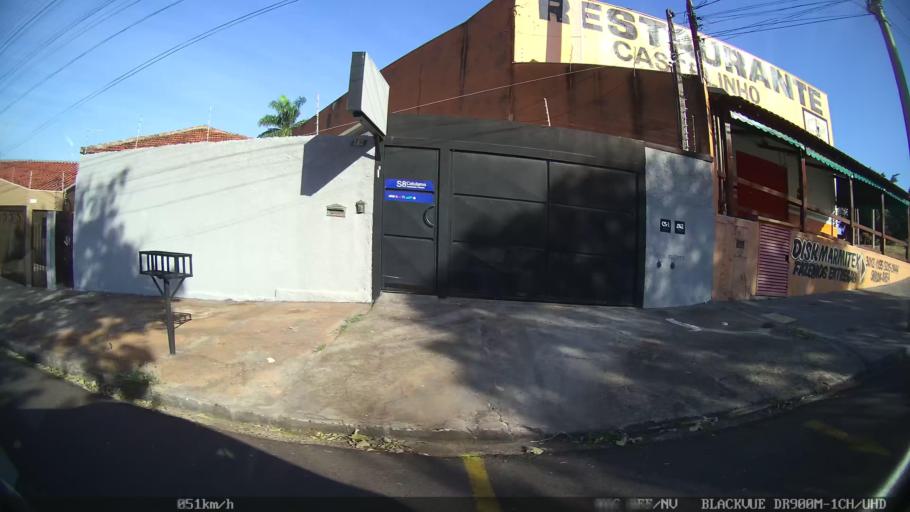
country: BR
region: Sao Paulo
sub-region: Sao Jose Do Rio Preto
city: Sao Jose do Rio Preto
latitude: -20.7800
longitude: -49.3626
